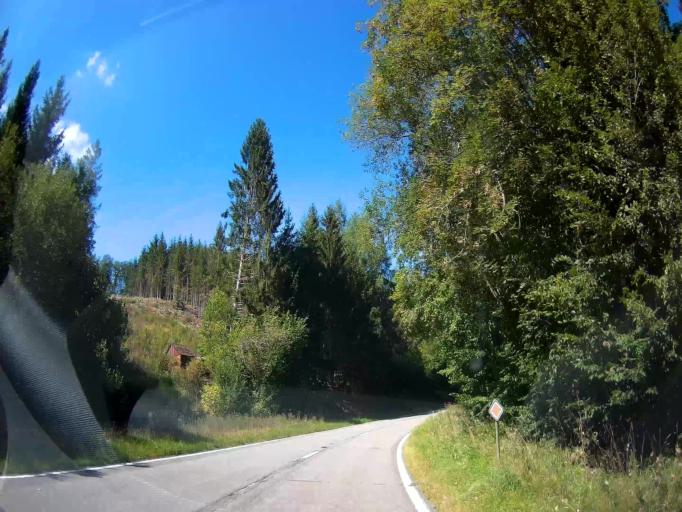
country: BE
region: Wallonia
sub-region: Province du Luxembourg
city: Bertogne
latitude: 50.1028
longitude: 5.6423
